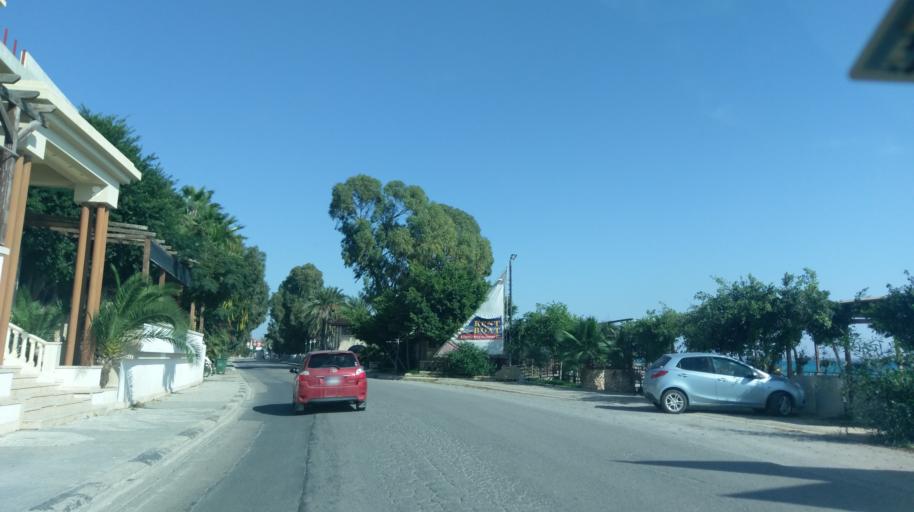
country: CY
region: Ammochostos
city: Trikomo
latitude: 35.3118
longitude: 33.9507
